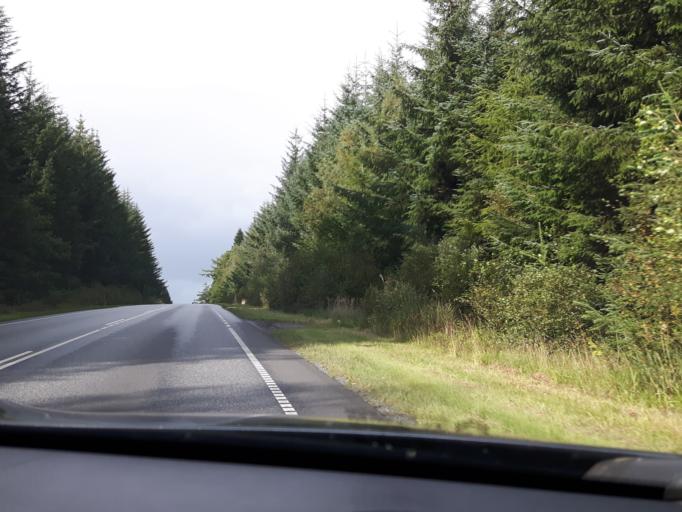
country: DK
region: North Denmark
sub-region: Jammerbugt Kommune
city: Fjerritslev
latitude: 57.0886
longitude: 9.3883
